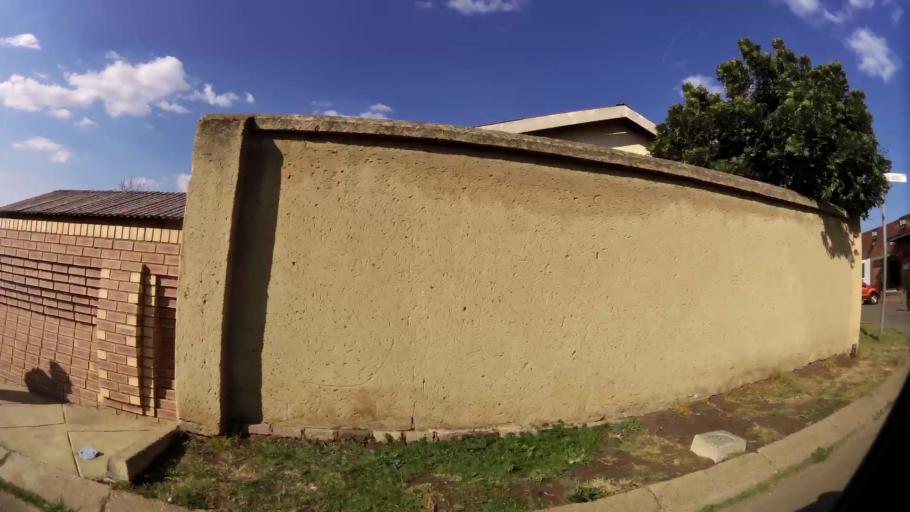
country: ZA
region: Gauteng
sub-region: City of Johannesburg Metropolitan Municipality
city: Soweto
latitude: -26.2256
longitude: 27.8773
